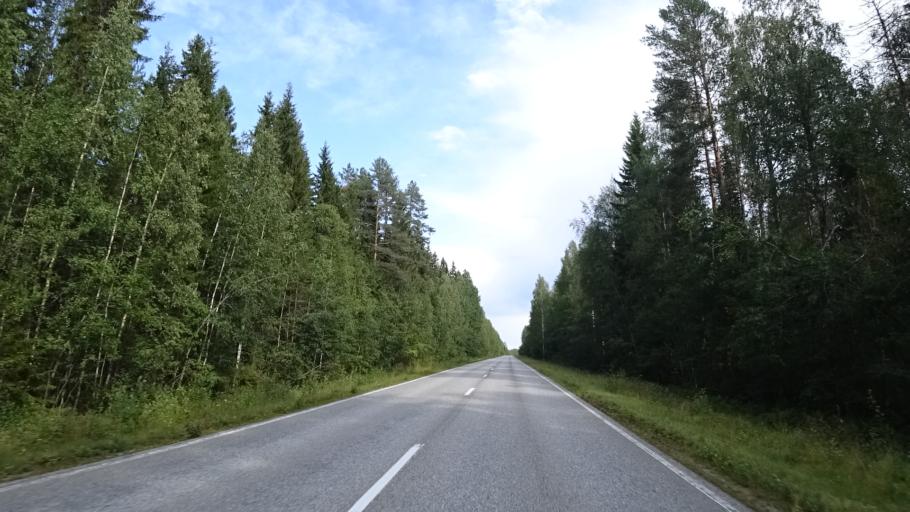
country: FI
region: North Karelia
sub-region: Joensuu
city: Ilomantsi
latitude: 62.6229
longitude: 31.1410
